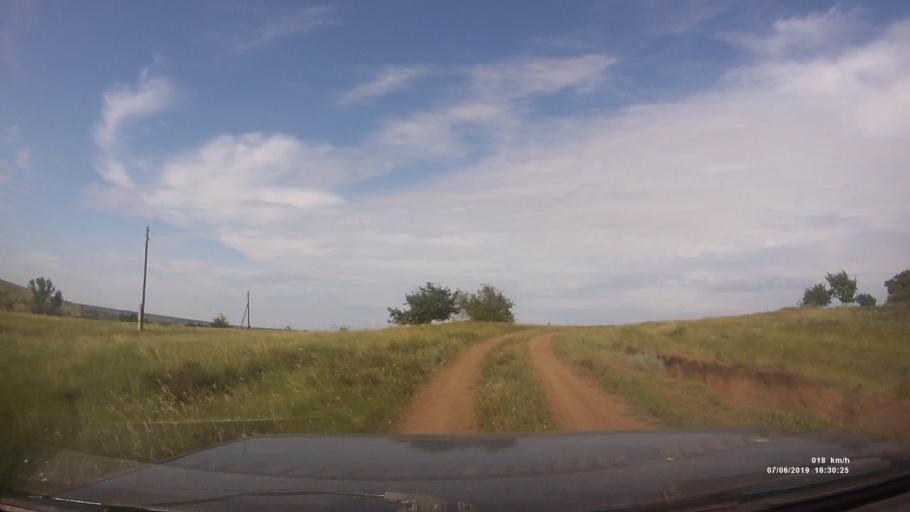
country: RU
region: Rostov
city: Staraya Stanitsa
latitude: 48.2557
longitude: 40.3232
